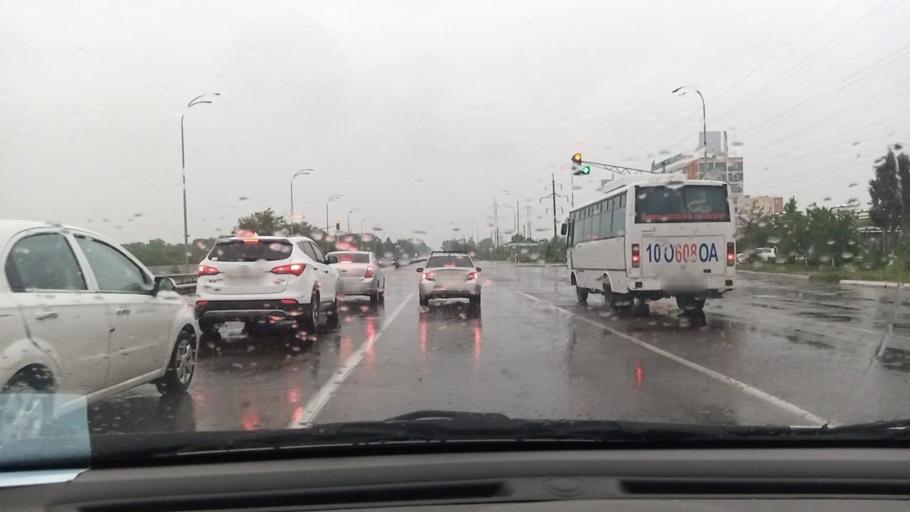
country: UZ
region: Toshkent Shahri
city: Bektemir
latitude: 41.2583
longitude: 69.3787
